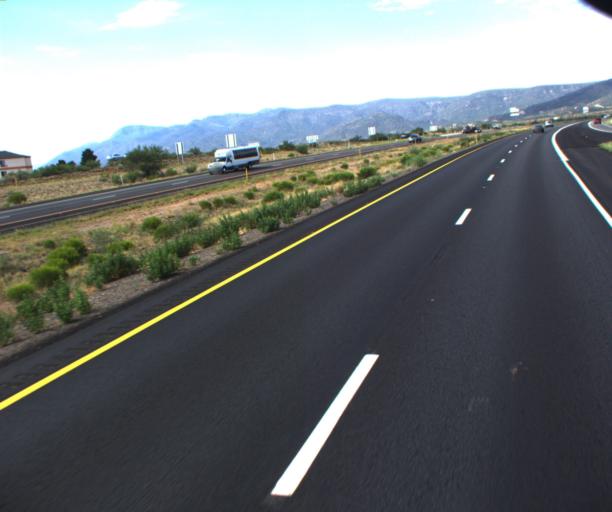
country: US
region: Arizona
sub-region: Yavapai County
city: Camp Verde
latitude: 34.5765
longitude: -111.8853
